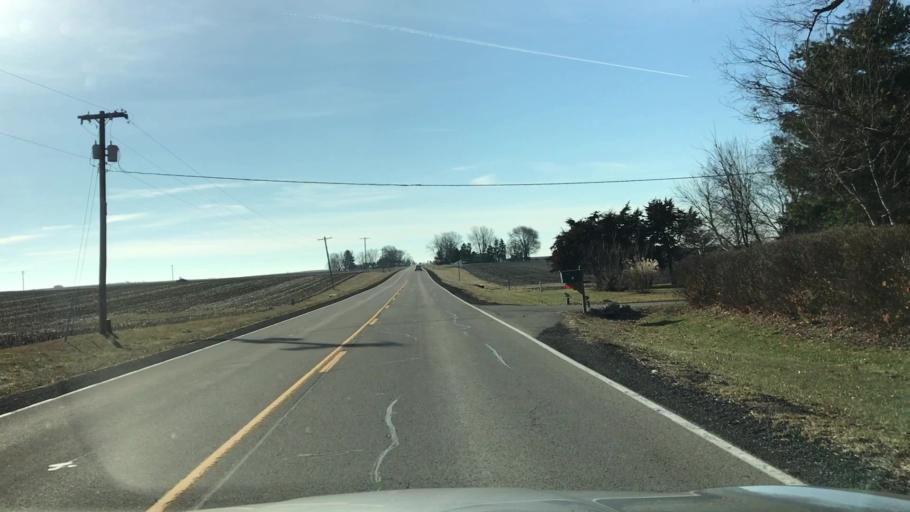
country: US
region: Illinois
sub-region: McLean County
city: Hudson
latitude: 40.6098
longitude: -88.9453
